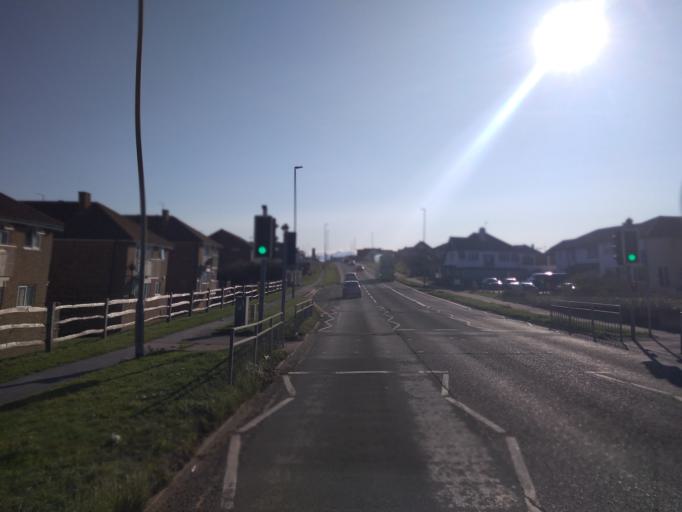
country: GB
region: England
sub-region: East Sussex
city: Peacehaven
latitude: 50.7953
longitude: -0.0201
